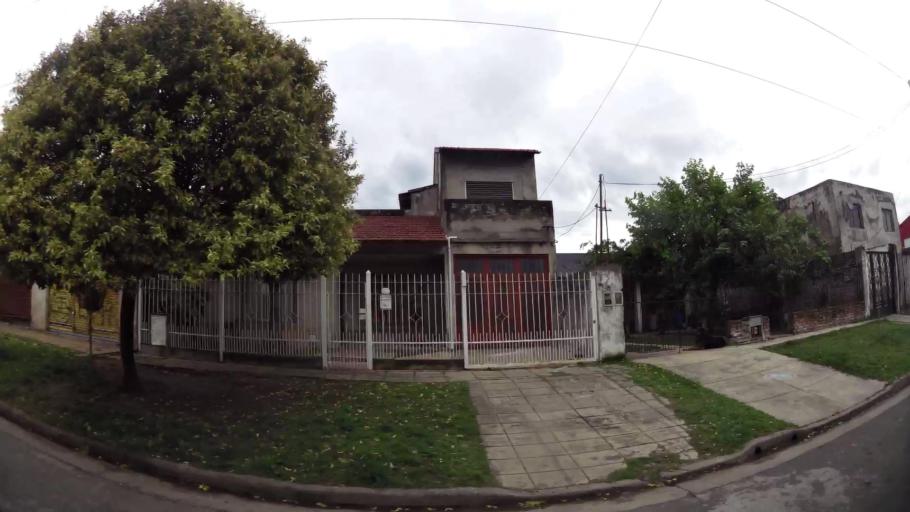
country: AR
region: Buenos Aires
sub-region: Partido de Lanus
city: Lanus
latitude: -34.7388
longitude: -58.3583
